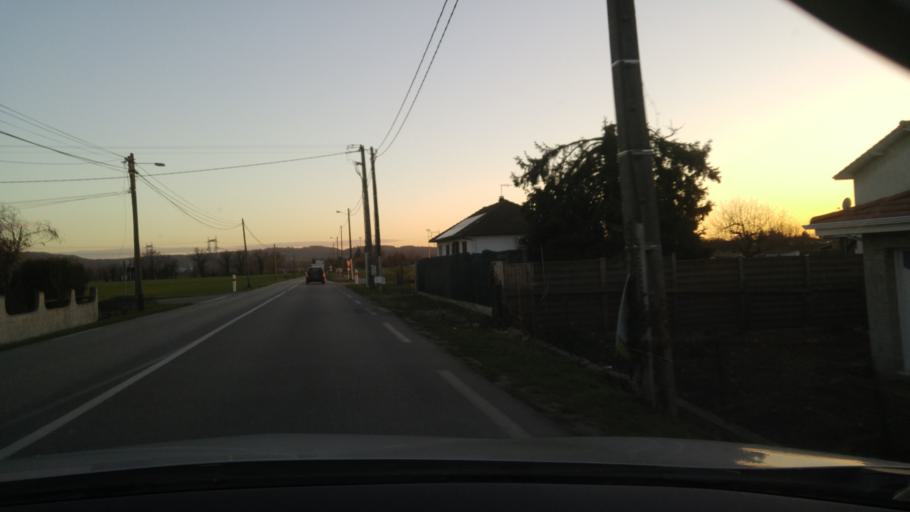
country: FR
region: Rhone-Alpes
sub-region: Departement de l'Isere
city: Tignieu-Jameyzieu
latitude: 45.7308
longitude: 5.1869
